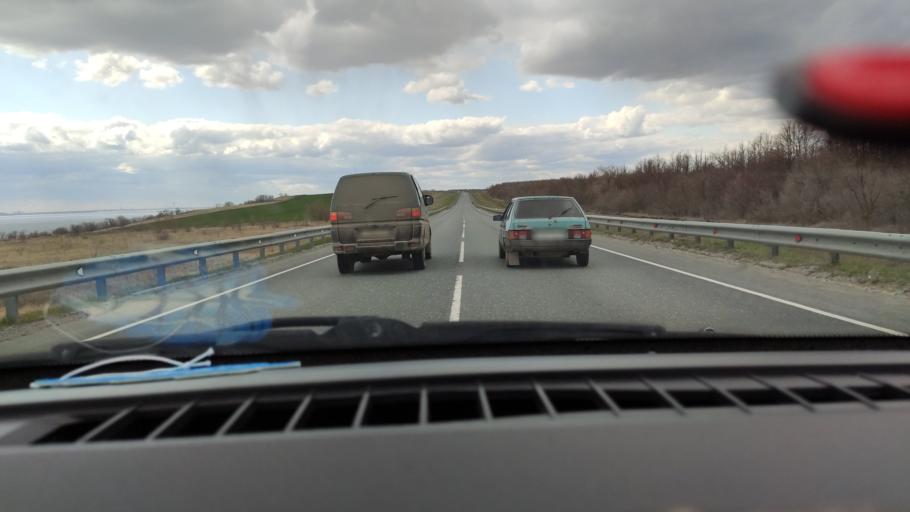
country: RU
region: Saratov
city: Balakovo
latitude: 52.1946
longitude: 47.8574
